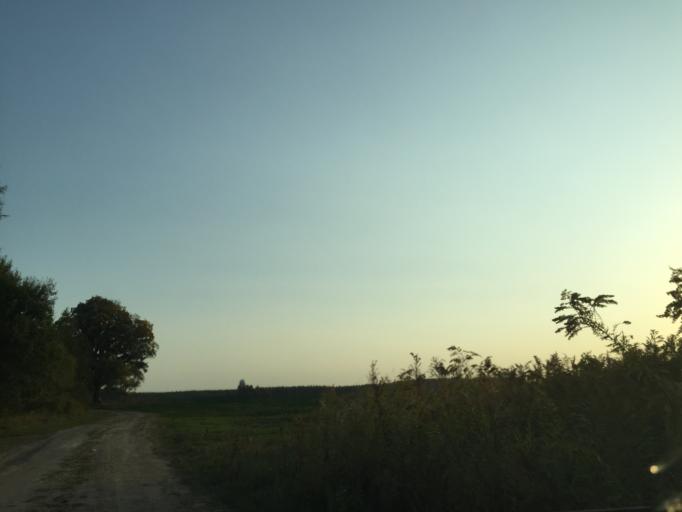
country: LV
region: Lielvarde
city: Lielvarde
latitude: 56.7866
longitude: 24.8147
